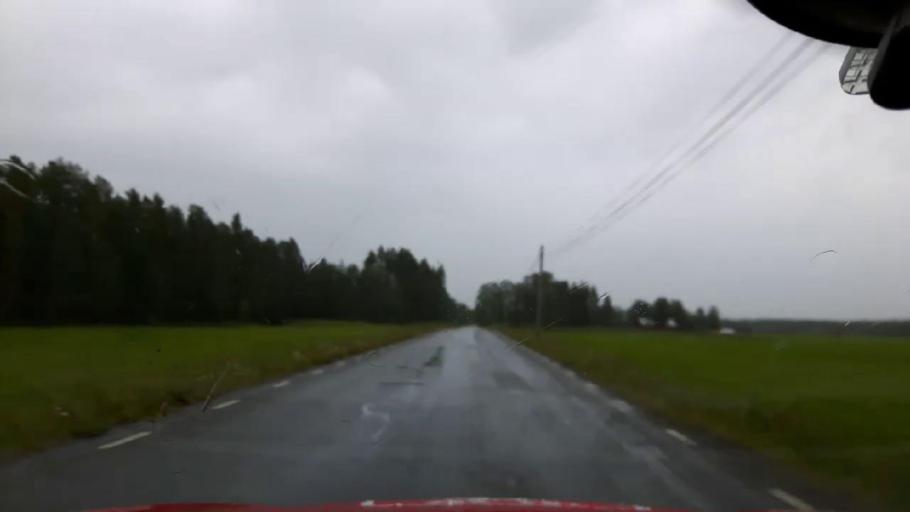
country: SE
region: Jaemtland
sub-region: OEstersunds Kommun
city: Brunflo
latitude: 62.9963
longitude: 14.7748
